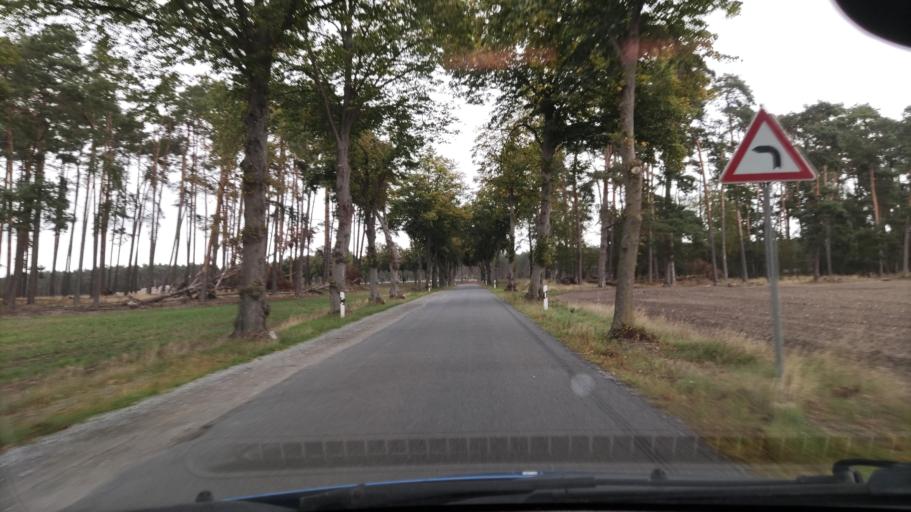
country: DE
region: Saxony-Anhalt
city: Luftkurort Arendsee
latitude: 52.9489
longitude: 11.5416
